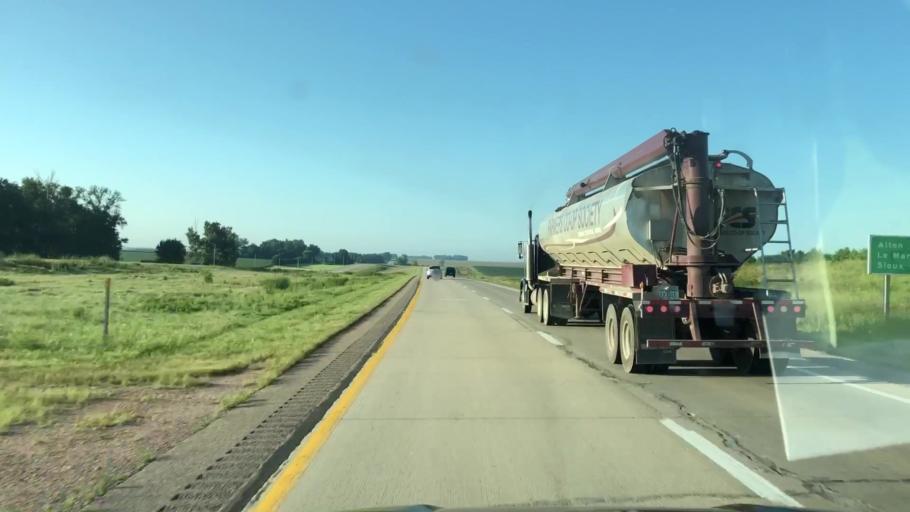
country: US
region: Iowa
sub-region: Sioux County
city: Alton
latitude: 43.0474
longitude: -95.9200
